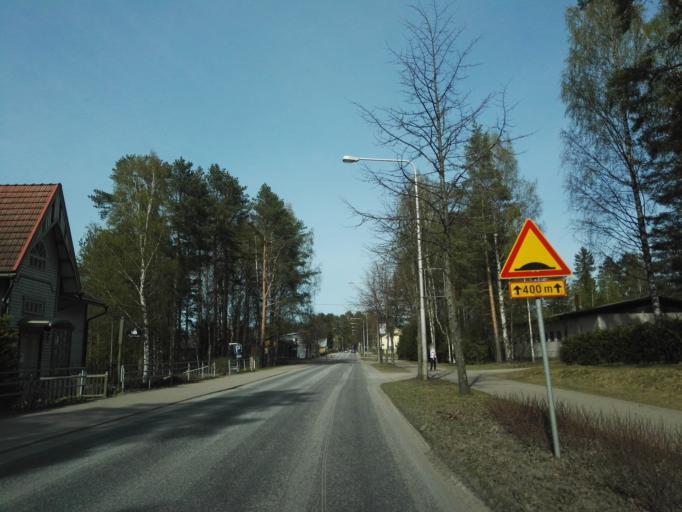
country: FI
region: Central Finland
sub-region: Joutsa
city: Joutsa
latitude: 61.7426
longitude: 26.1159
